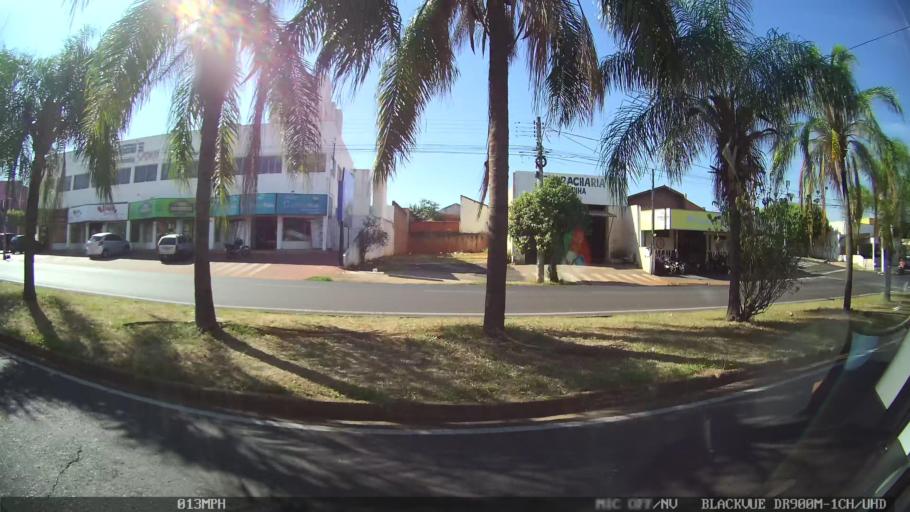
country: BR
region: Sao Paulo
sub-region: Sao Jose Do Rio Preto
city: Sao Jose do Rio Preto
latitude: -20.7860
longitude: -49.3686
